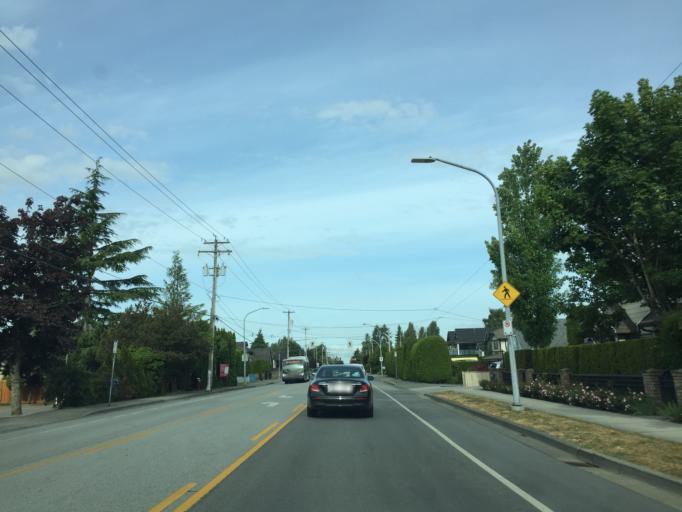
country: CA
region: British Columbia
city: Richmond
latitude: 49.1411
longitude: -123.1767
